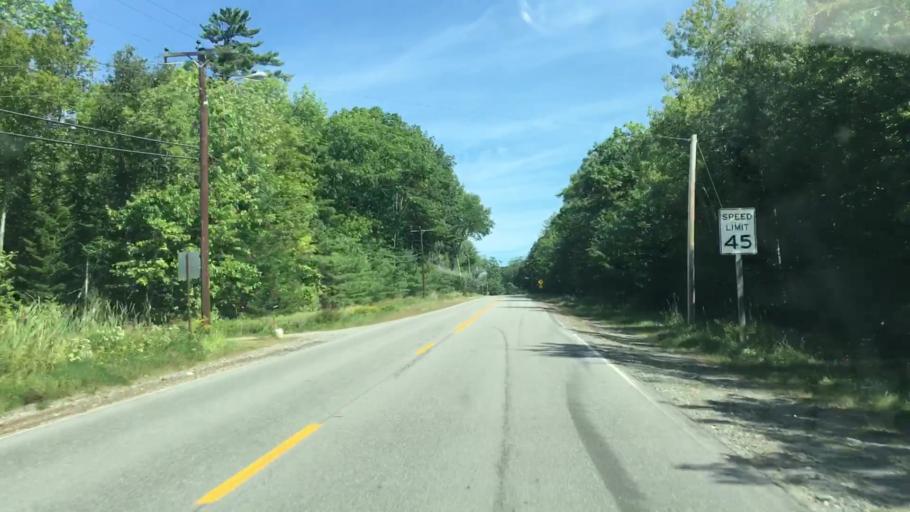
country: US
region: Maine
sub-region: Penobscot County
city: Bradford
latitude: 45.1766
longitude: -68.8591
